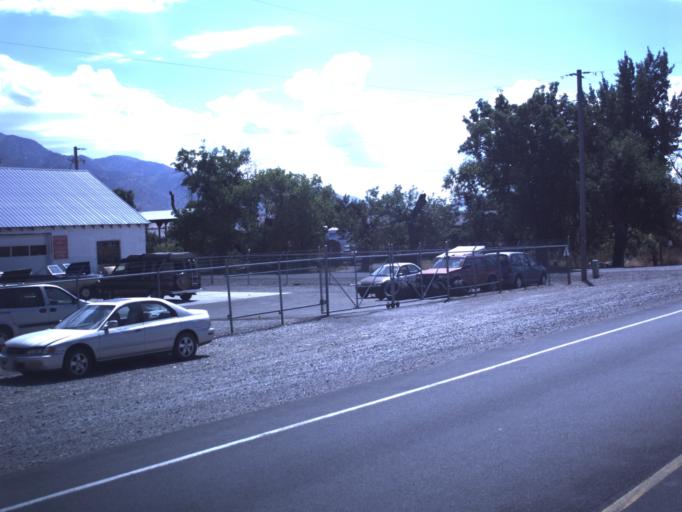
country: US
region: Utah
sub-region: Box Elder County
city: Elwood
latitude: 41.6909
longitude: -112.1416
